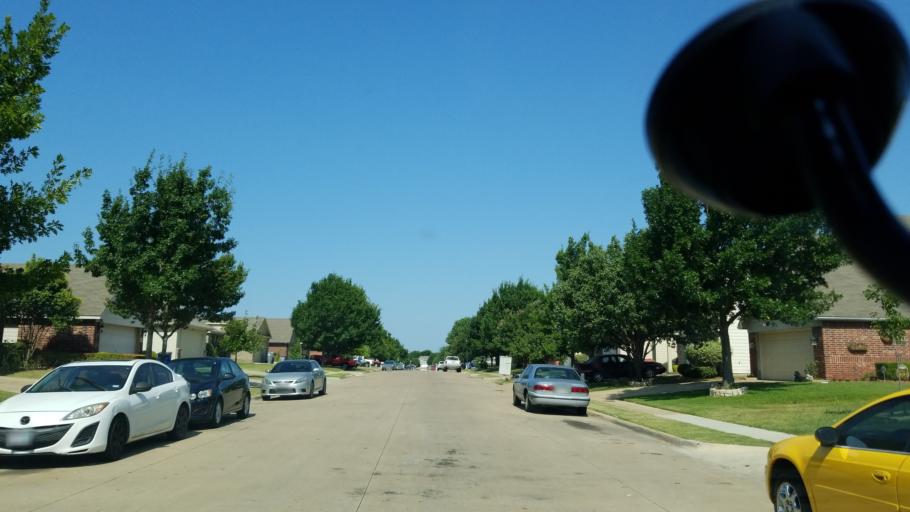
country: US
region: Texas
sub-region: Dallas County
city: Cockrell Hill
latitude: 32.7127
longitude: -96.8666
